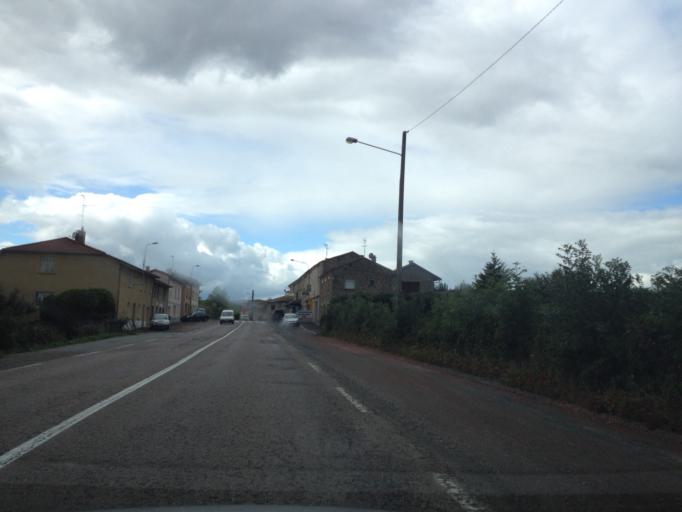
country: FR
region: Rhone-Alpes
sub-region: Departement de la Loire
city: Saint-Symphorien-de-Lay
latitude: 45.9615
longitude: 4.1810
